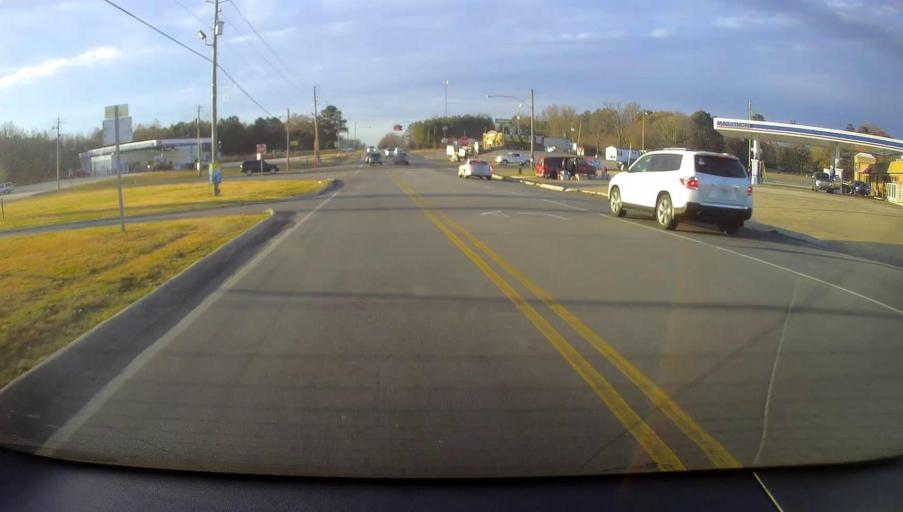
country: US
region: Alabama
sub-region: Blount County
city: Oneonta
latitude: 34.1194
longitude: -86.3946
